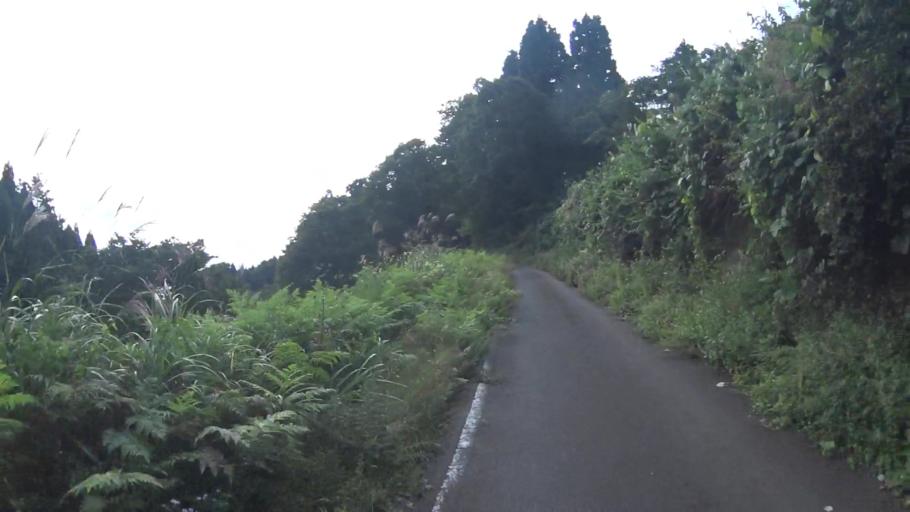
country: JP
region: Kyoto
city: Miyazu
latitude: 35.6404
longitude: 135.1809
